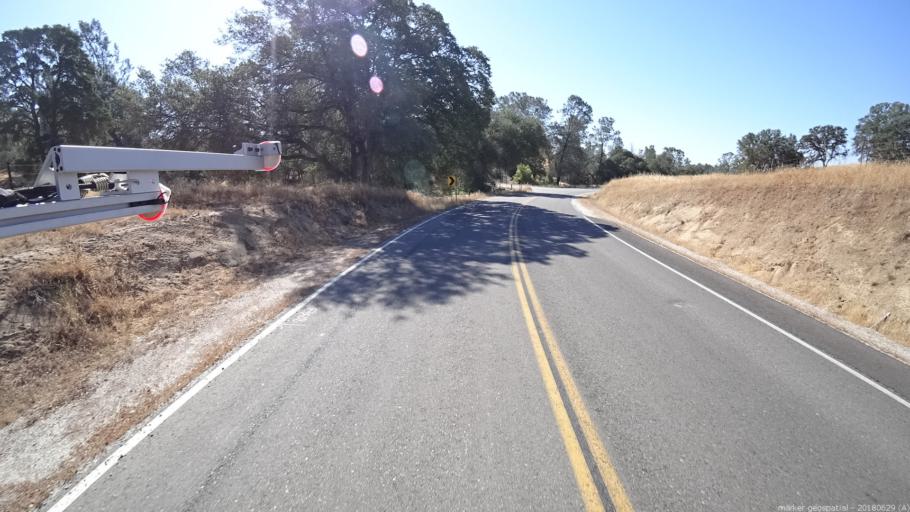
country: US
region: California
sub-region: Madera County
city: Yosemite Lakes
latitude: 37.0835
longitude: -119.7957
